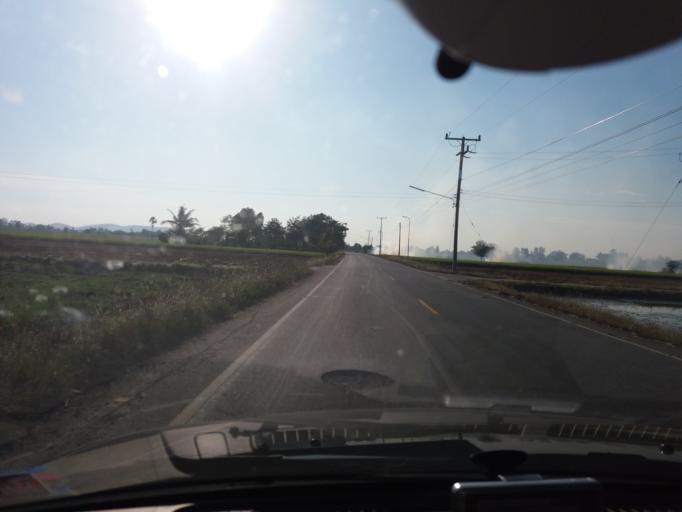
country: TH
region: Suphan Buri
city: Doem Bang Nang Buat
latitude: 14.9161
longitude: 100.1554
